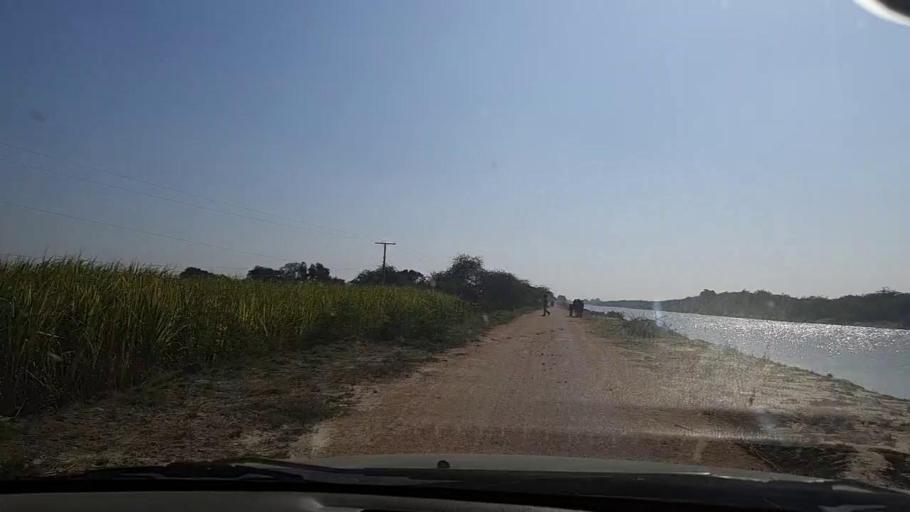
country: PK
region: Sindh
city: Thatta
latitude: 24.6033
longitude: 68.0507
